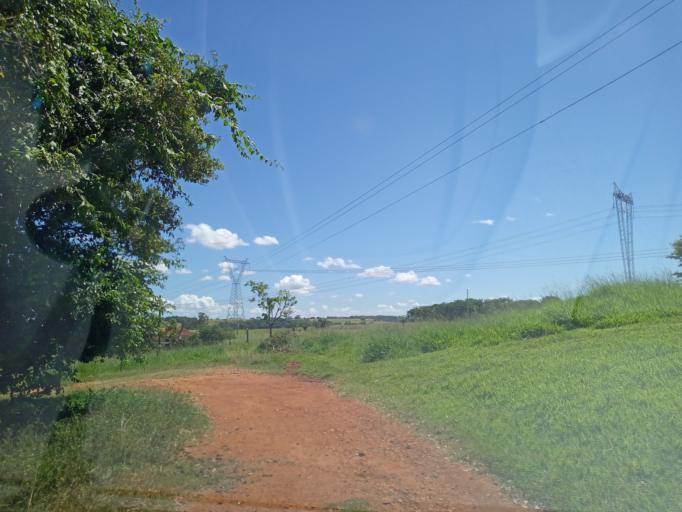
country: BR
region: Goias
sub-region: Itumbiara
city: Itumbiara
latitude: -18.3967
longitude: -49.1258
